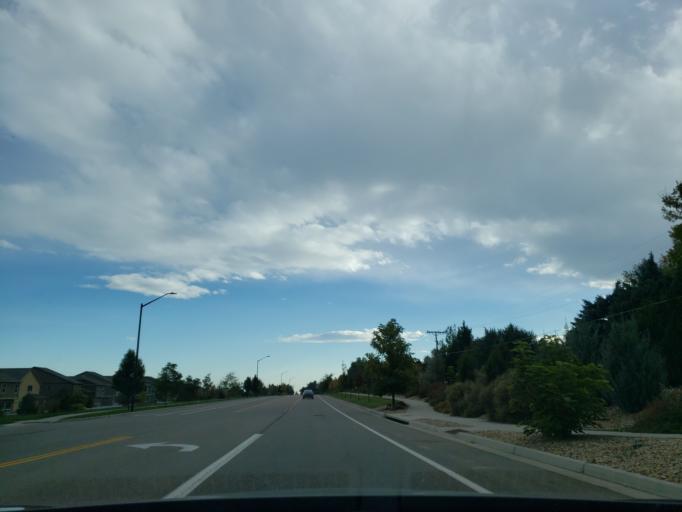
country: US
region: Colorado
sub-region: Larimer County
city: Fort Collins
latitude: 40.6214
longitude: -105.0388
